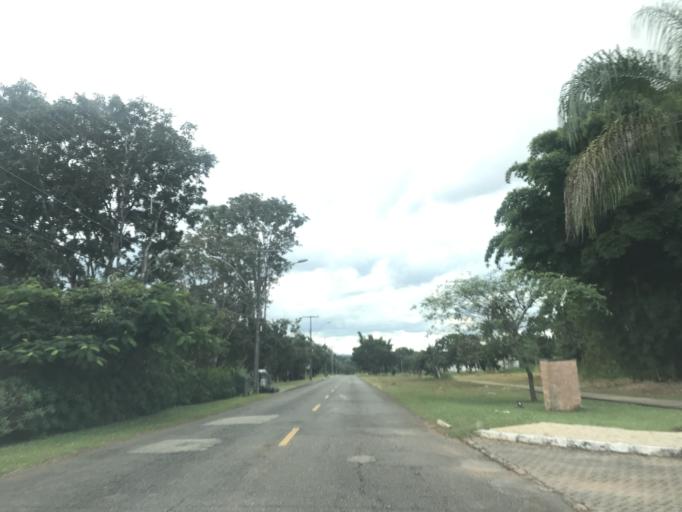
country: BR
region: Federal District
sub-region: Brasilia
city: Brasilia
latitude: -15.9023
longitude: -47.9392
